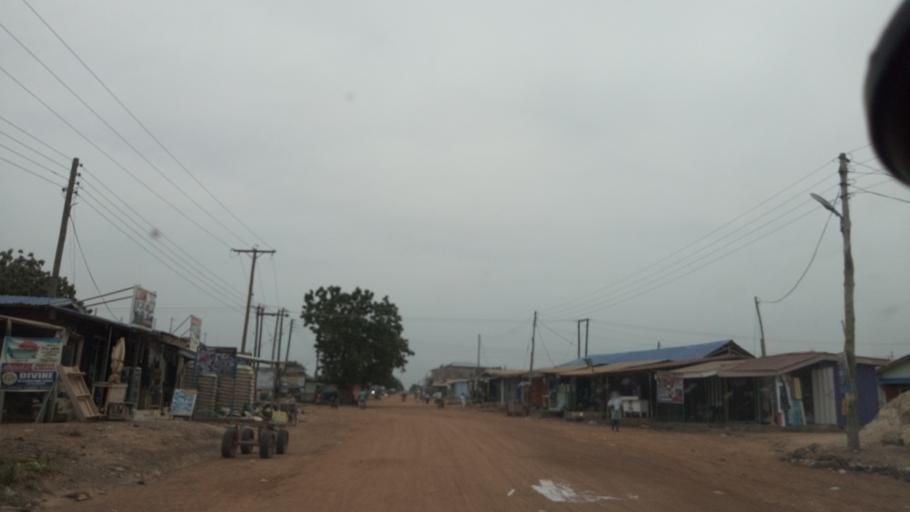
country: GH
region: Greater Accra
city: Medina Estates
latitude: 5.7089
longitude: -0.1307
